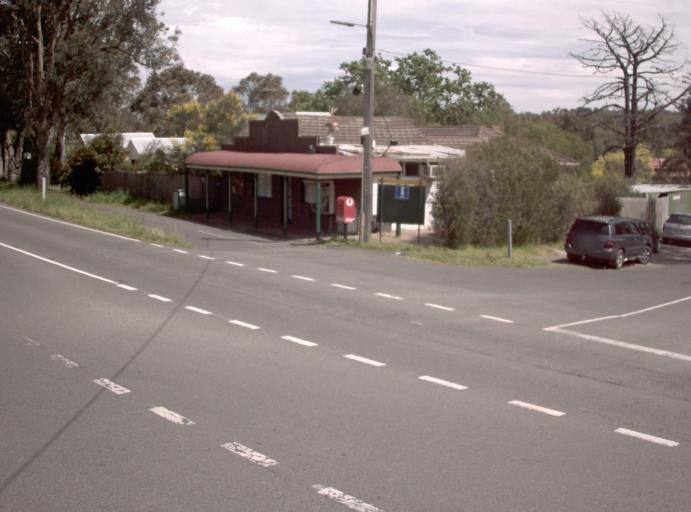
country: AU
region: Victoria
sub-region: Manningham
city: Warrandyte
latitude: -37.7605
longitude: 145.2342
